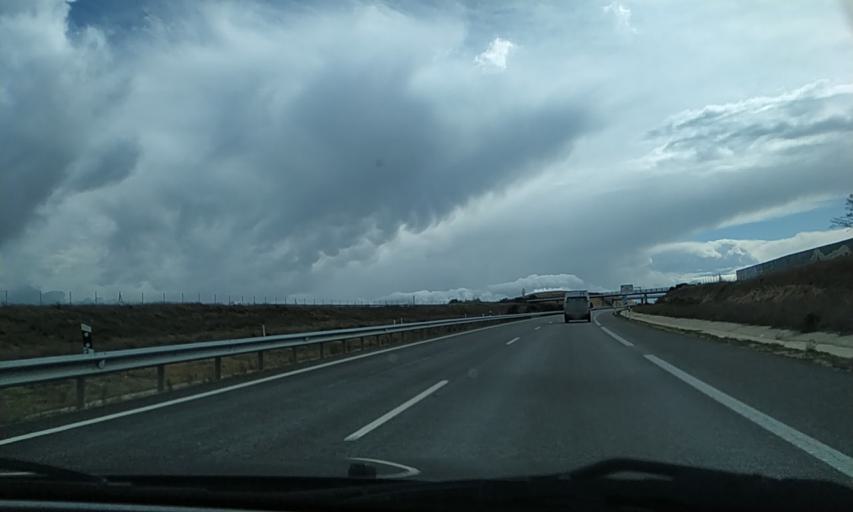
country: ES
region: Castille and Leon
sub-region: Provincia de Salamanca
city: Monterrubio de Armuna
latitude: 41.0355
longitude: -5.6696
